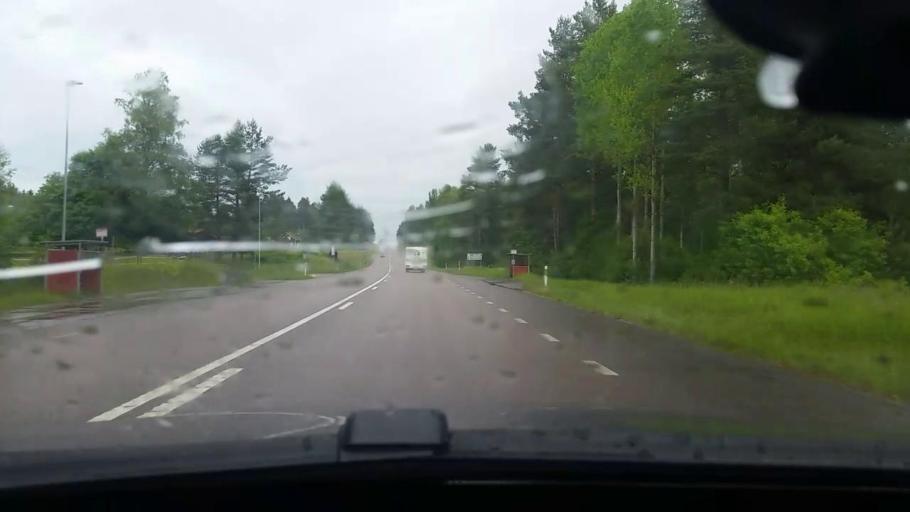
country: SE
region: Dalarna
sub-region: Gagnefs Kommun
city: Gagnef
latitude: 60.6330
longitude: 15.0577
